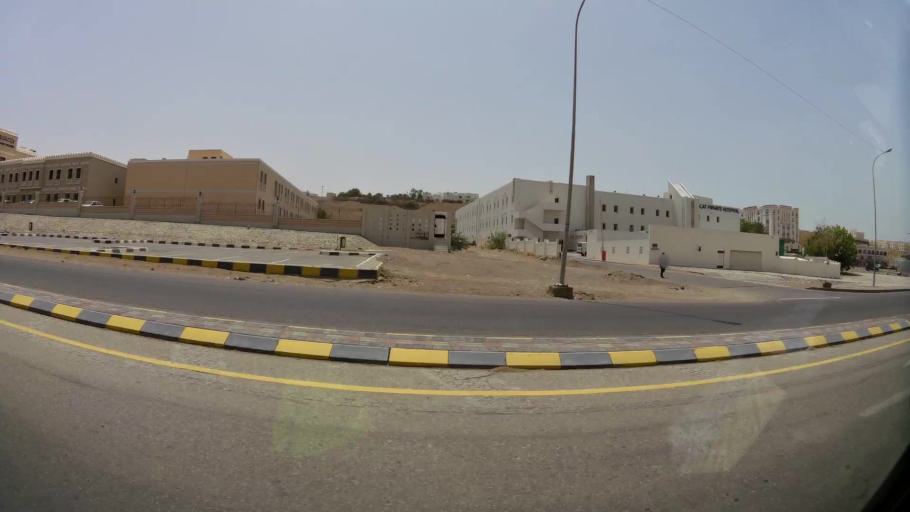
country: OM
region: Muhafazat Masqat
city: Bawshar
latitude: 23.5487
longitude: 58.3988
